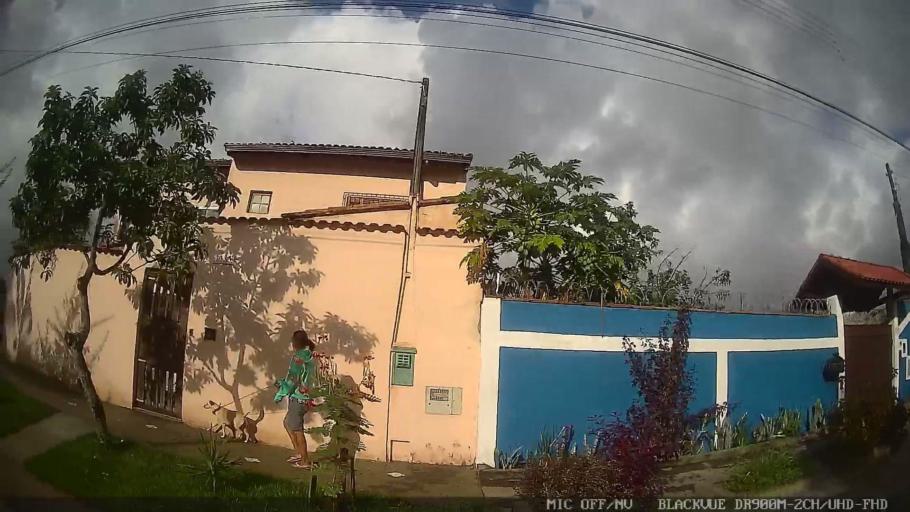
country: BR
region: Sao Paulo
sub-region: Itanhaem
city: Itanhaem
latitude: -24.1954
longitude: -46.8664
